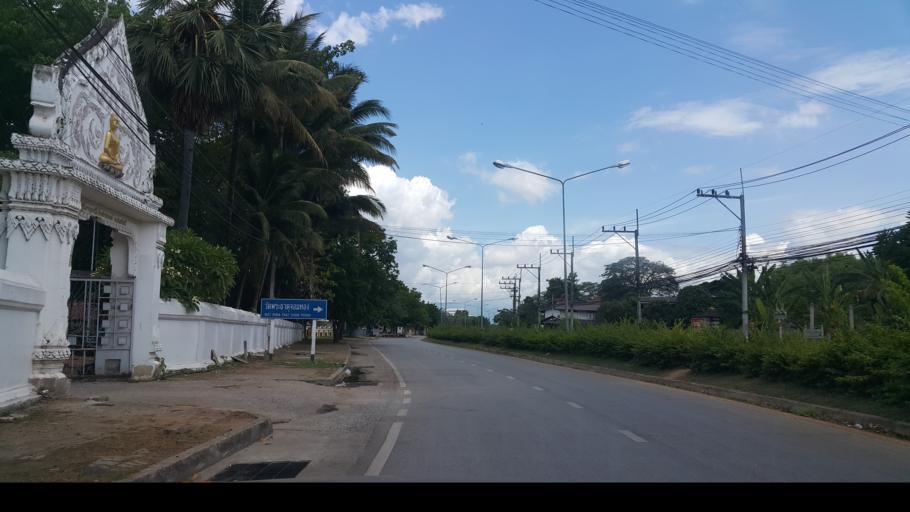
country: TH
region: Phayao
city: Phayao
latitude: 19.1776
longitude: 99.8893
